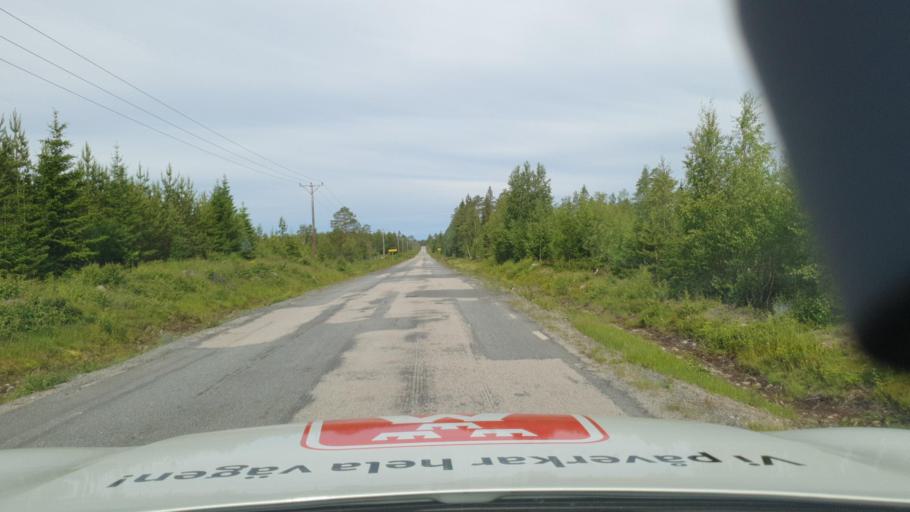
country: SE
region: Vaesterbotten
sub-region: Umea Kommun
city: Saevar
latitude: 63.8685
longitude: 20.7283
